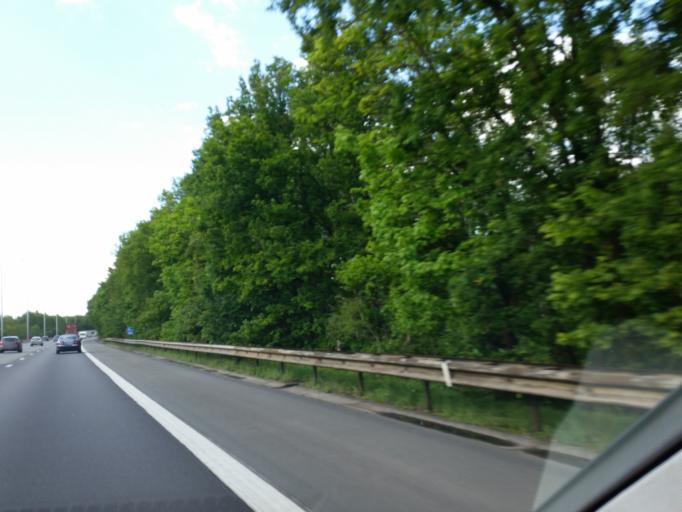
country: BE
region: Flanders
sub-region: Provincie Antwerpen
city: Rumst
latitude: 51.0656
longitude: 4.4460
